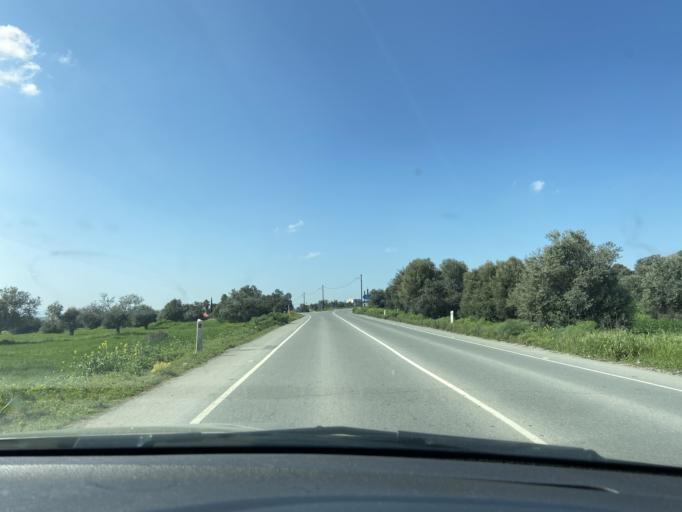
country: CY
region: Lefkosia
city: Dali
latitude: 35.0253
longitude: 33.3882
